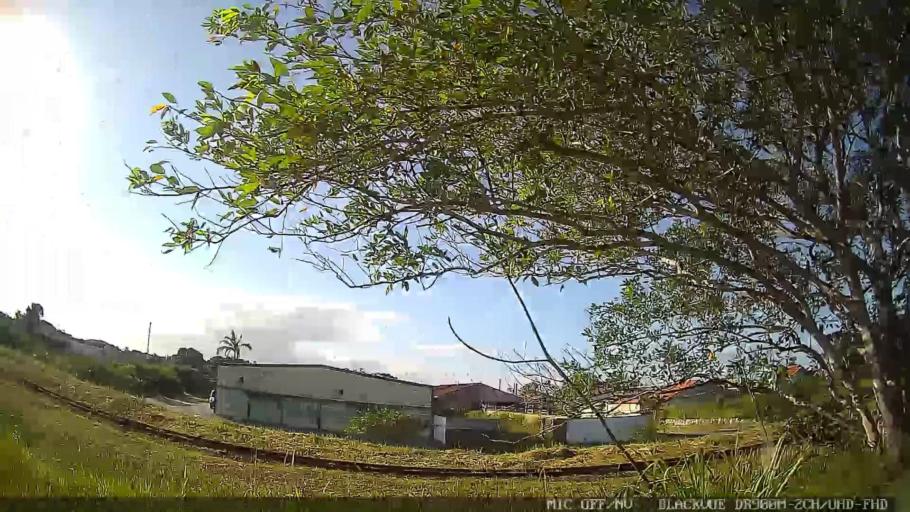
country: BR
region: Sao Paulo
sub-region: Peruibe
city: Peruibe
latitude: -24.2823
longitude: -46.9620
